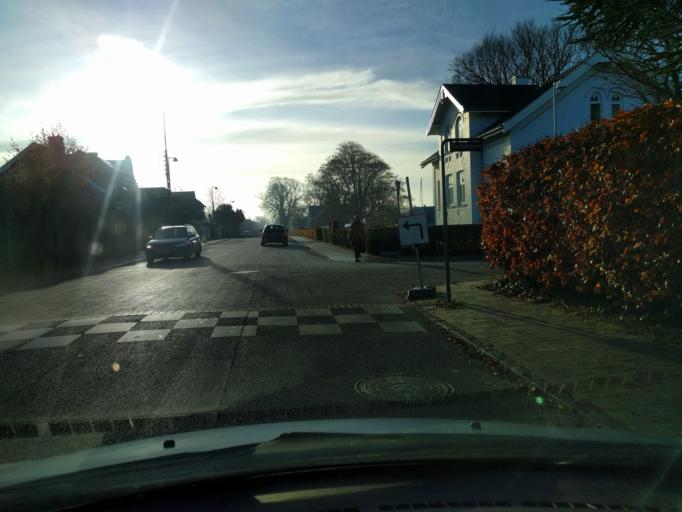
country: DK
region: South Denmark
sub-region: Odense Kommune
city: Odense
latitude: 55.3871
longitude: 10.3891
